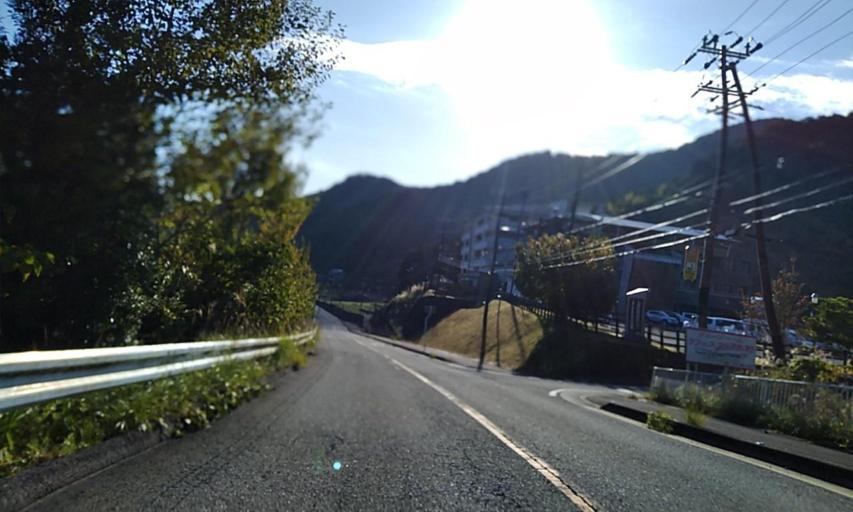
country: JP
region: Wakayama
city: Iwade
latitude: 34.1528
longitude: 135.3100
